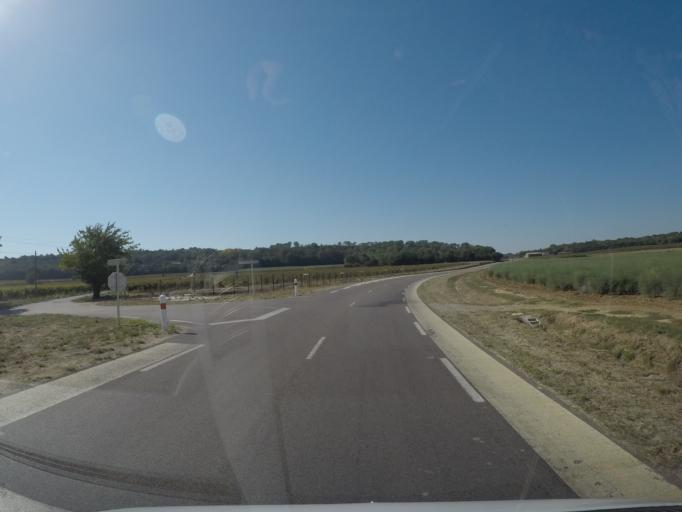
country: FR
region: Languedoc-Roussillon
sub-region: Departement du Gard
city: Uzes
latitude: 43.9942
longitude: 4.3921
